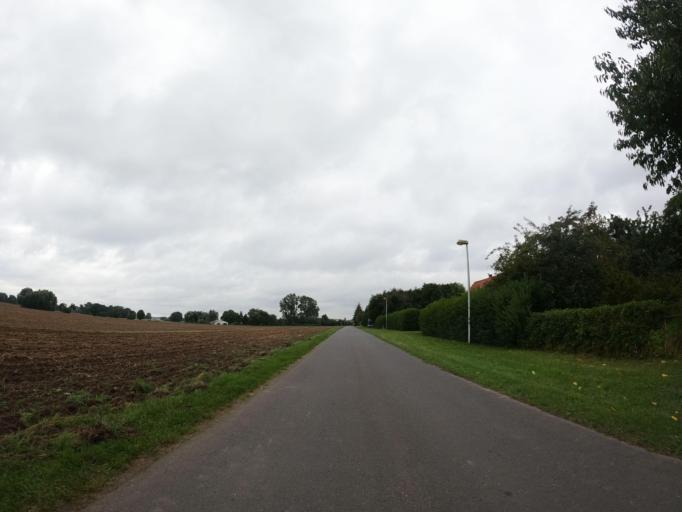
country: DE
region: Mecklenburg-Vorpommern
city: Poseritz
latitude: 54.2740
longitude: 13.2541
